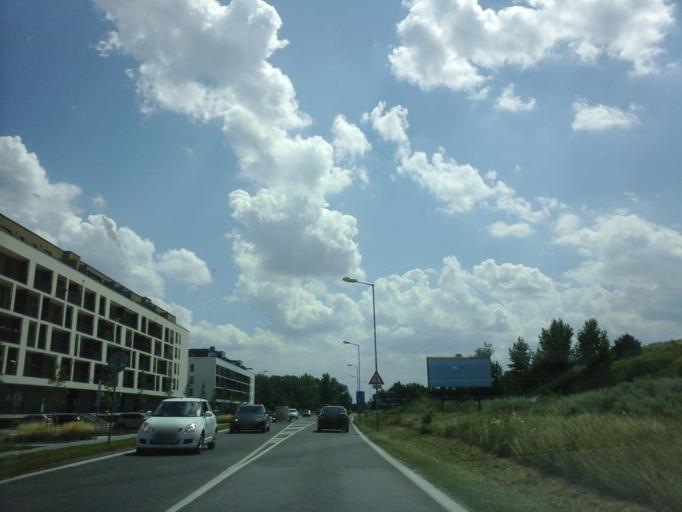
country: AT
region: Burgenland
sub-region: Politischer Bezirk Neusiedl am See
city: Kittsee
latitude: 48.0883
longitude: 17.1234
